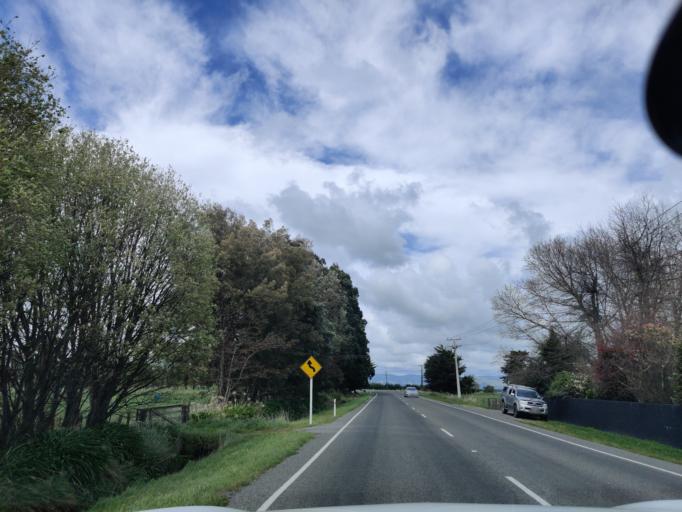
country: NZ
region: Manawatu-Wanganui
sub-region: Palmerston North City
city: Palmerston North
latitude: -40.3267
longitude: 175.5062
